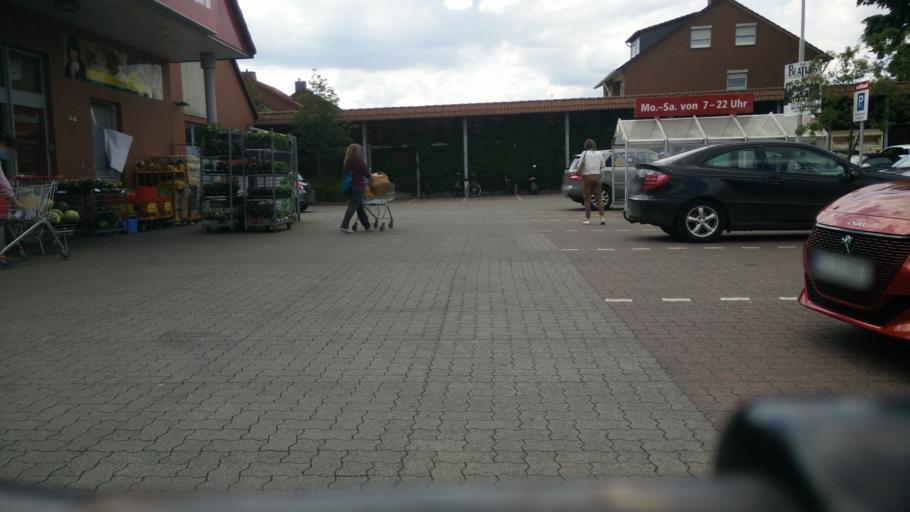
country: DE
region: Lower Saxony
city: Wunstorf
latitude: 52.4245
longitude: 9.4676
